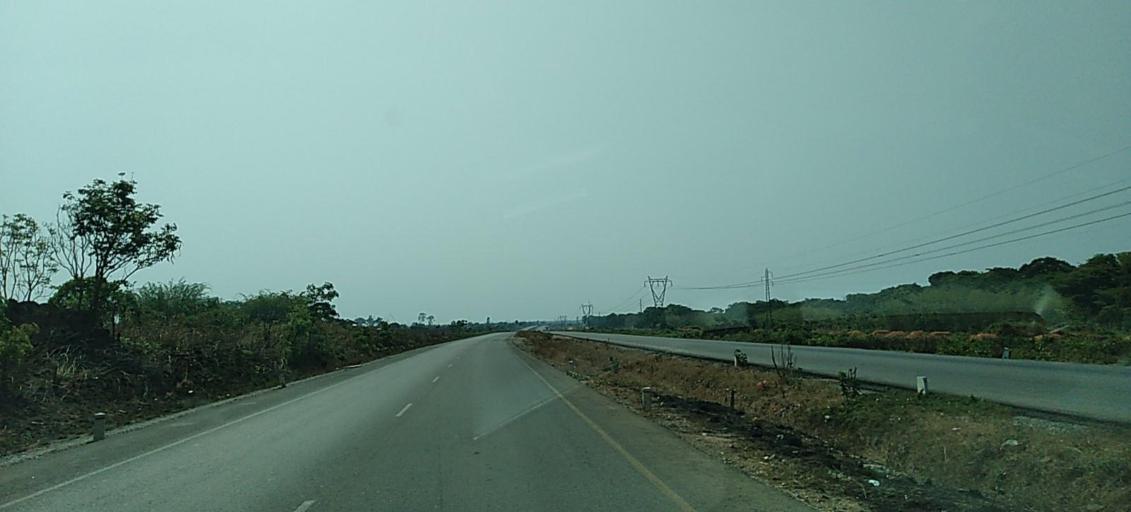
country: ZM
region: Copperbelt
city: Chingola
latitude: -12.5842
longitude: 27.9342
